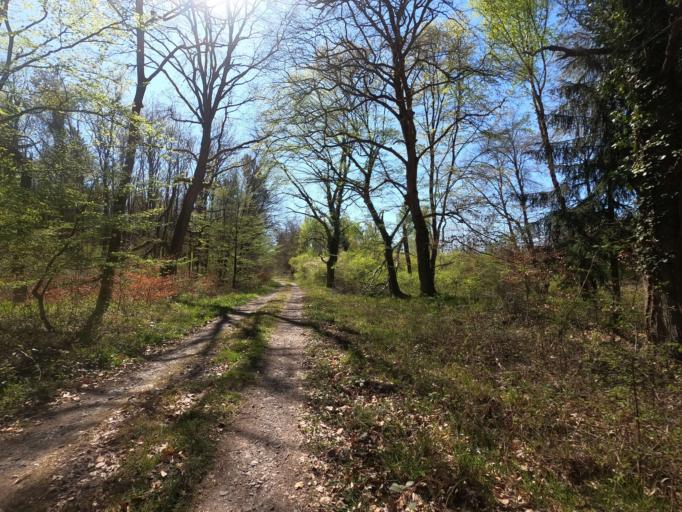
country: DE
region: Hesse
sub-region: Regierungsbezirk Darmstadt
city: Buttelborn
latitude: 49.9401
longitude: 8.5211
